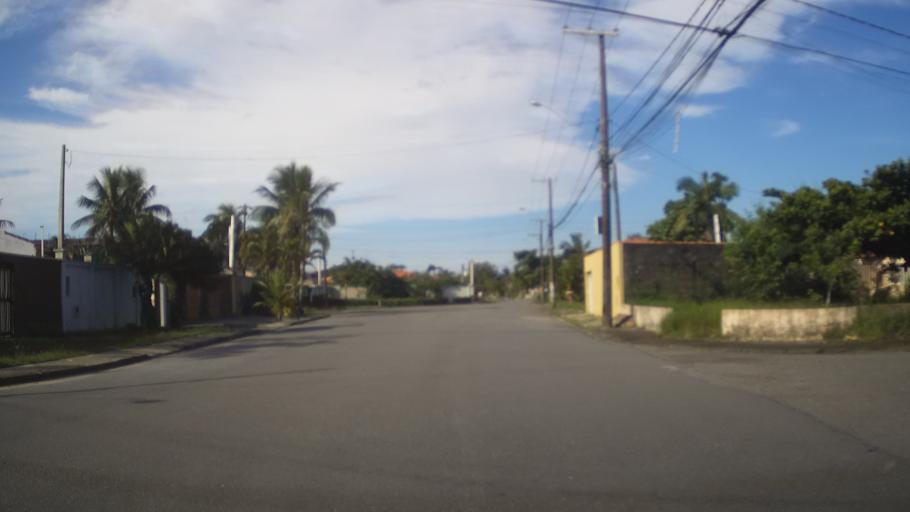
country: BR
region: Sao Paulo
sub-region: Itanhaem
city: Itanhaem
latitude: -24.1613
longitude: -46.7462
